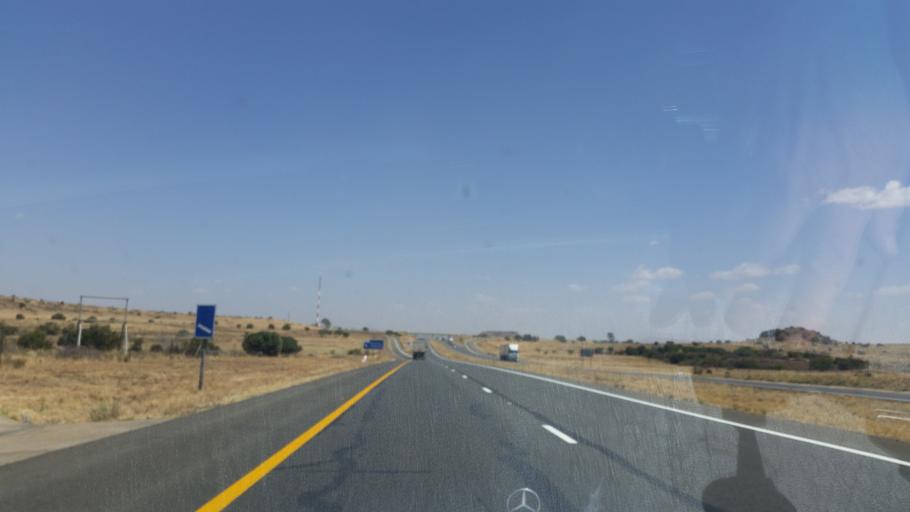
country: ZA
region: Orange Free State
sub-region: Lejweleputswa District Municipality
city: Brandfort
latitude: -28.9297
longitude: 26.4274
